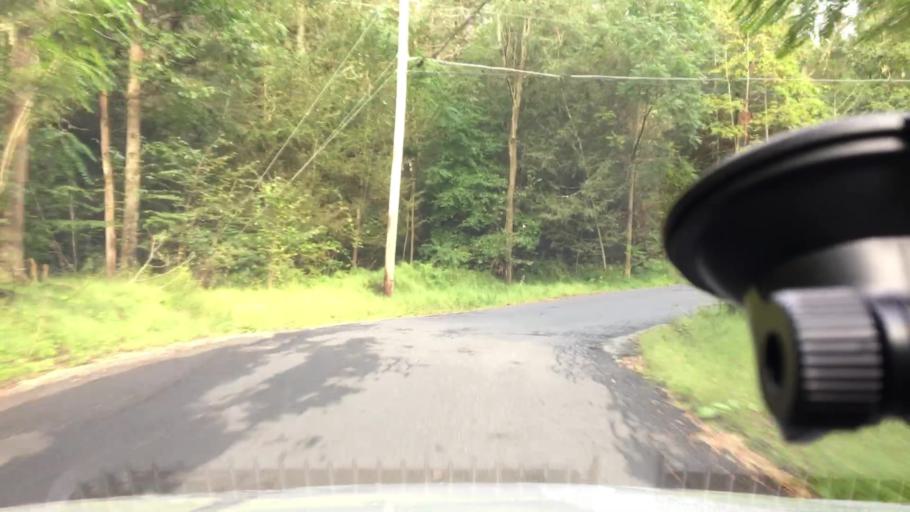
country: US
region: Pennsylvania
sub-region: Monroe County
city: Mountainhome
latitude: 41.1603
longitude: -75.2625
